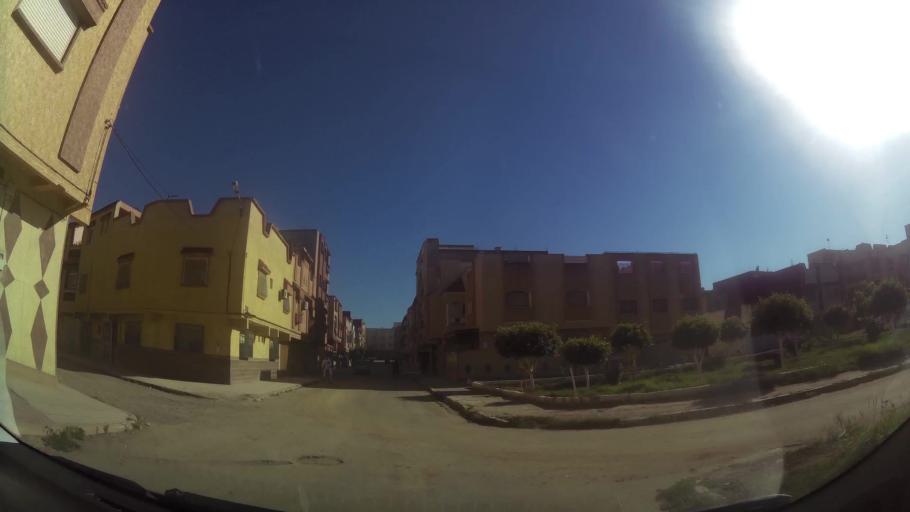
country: MA
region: Oriental
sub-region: Berkane-Taourirt
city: Ahfir
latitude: 34.9577
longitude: -2.1032
